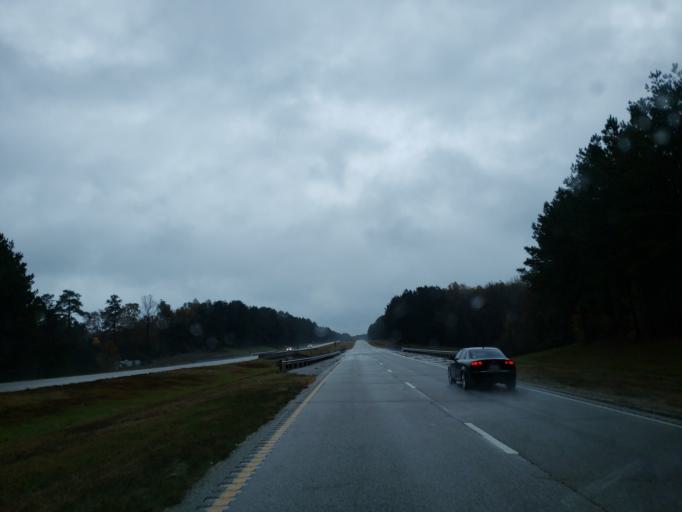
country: US
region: Mississippi
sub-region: Lauderdale County
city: Meridian
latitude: 32.2885
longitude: -88.6978
